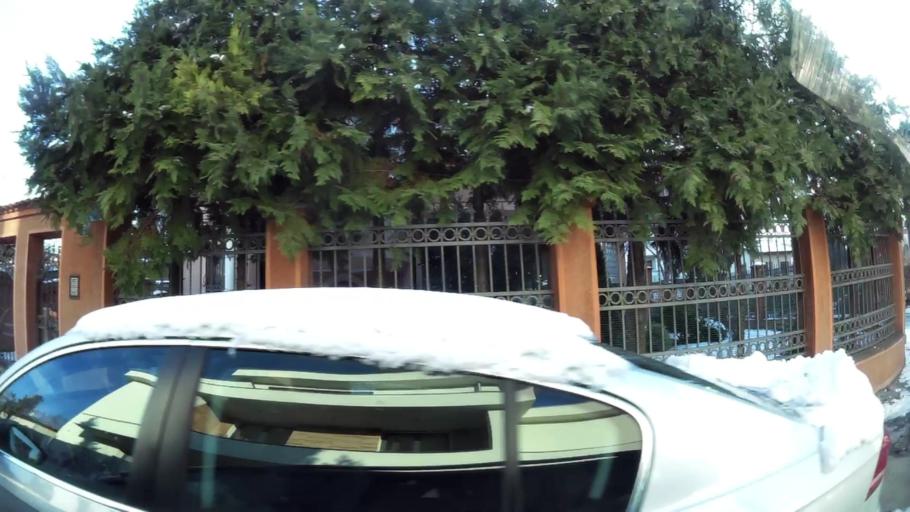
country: MK
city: Krushopek
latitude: 42.0025
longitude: 21.3883
